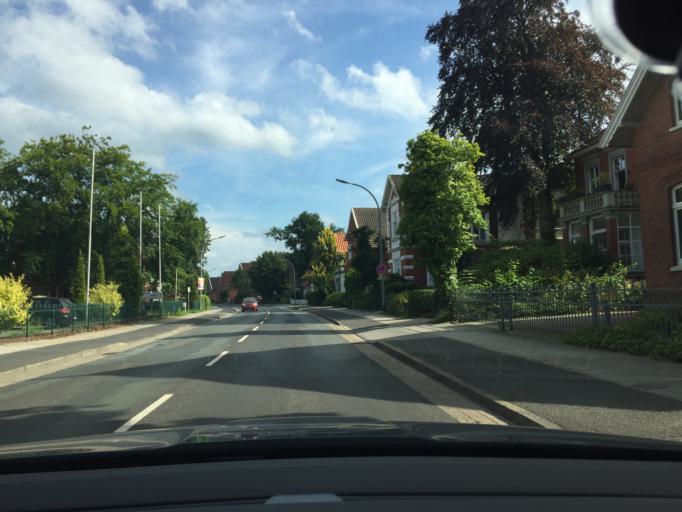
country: DE
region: Lower Saxony
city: Aurich
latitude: 53.4667
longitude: 7.4803
